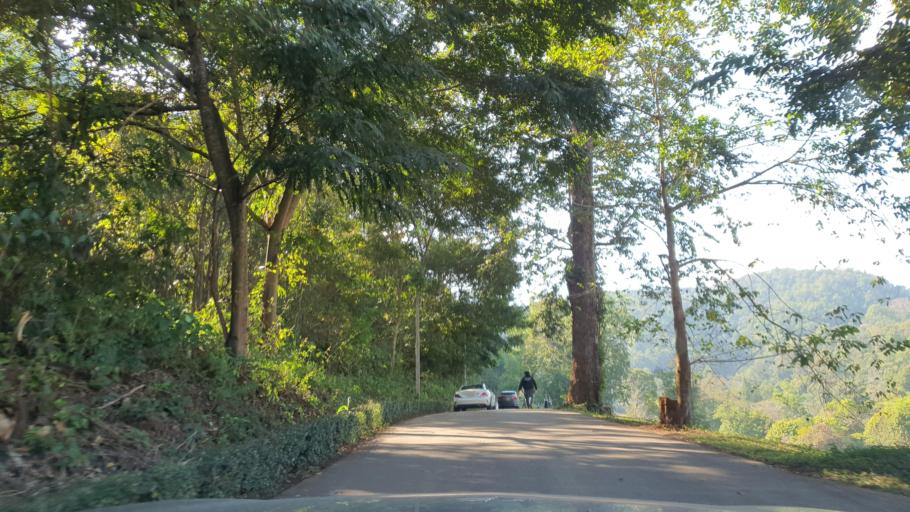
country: TH
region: Chiang Mai
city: Samoeng
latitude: 18.9003
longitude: 98.8273
